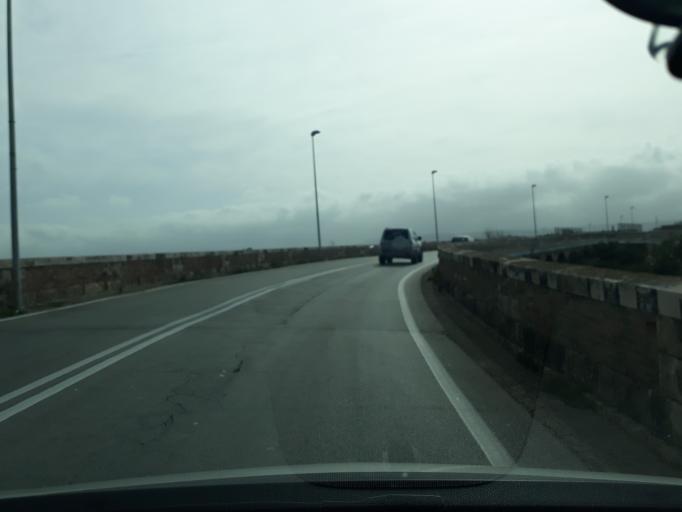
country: IT
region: Apulia
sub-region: Provincia di Bari
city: Monopoli
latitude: 40.9577
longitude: 17.2827
